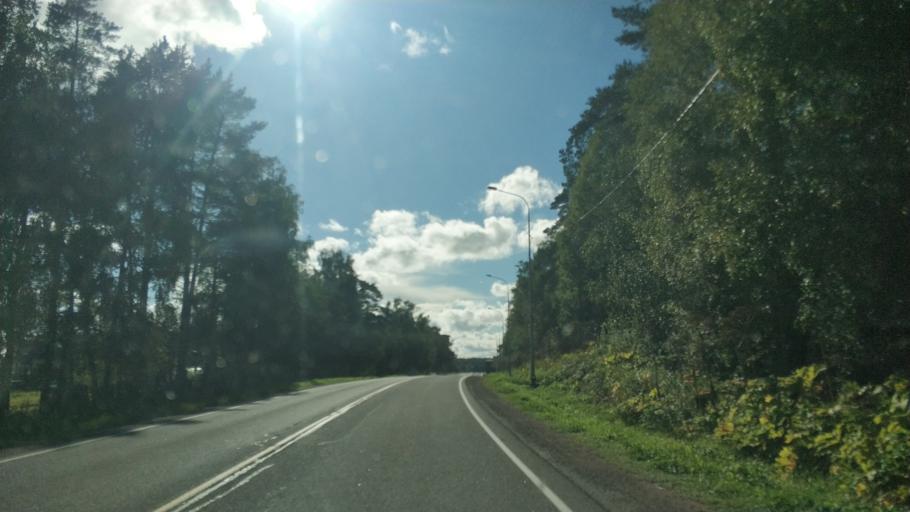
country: RU
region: Republic of Karelia
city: Khelyulya
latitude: 61.6499
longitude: 30.5992
